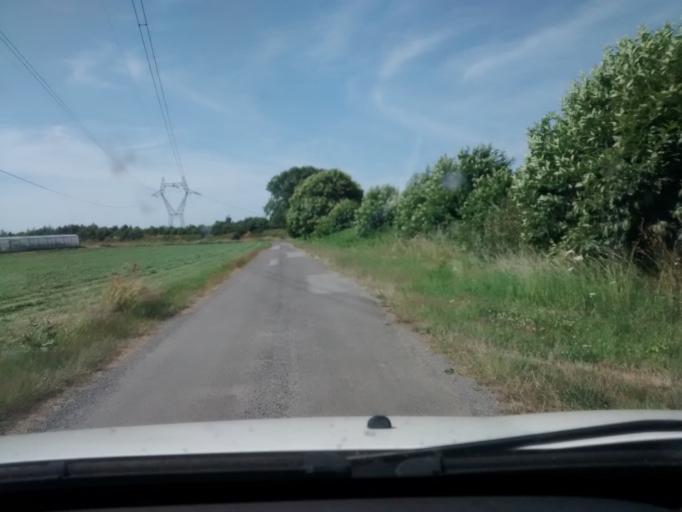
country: FR
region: Brittany
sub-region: Departement d'Ille-et-Vilaine
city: Acigne
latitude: 48.1122
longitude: -1.5586
